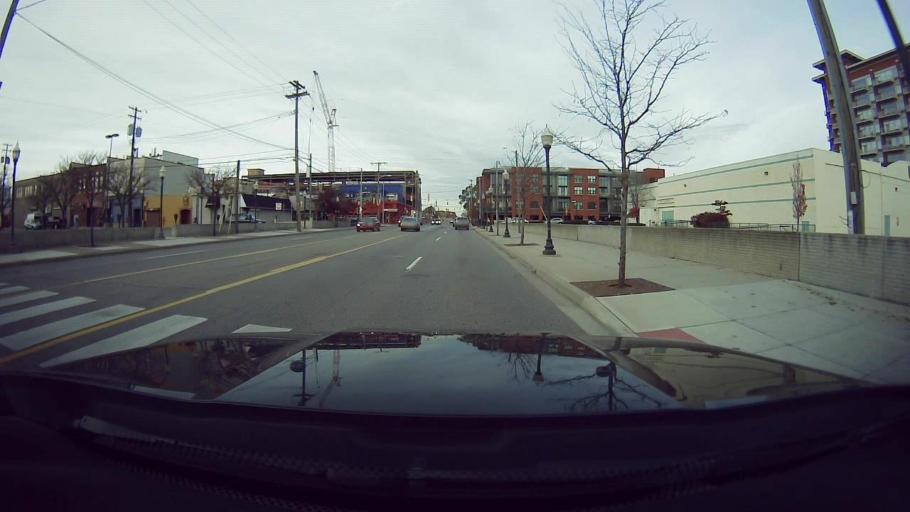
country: US
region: Michigan
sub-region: Oakland County
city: Royal Oak
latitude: 42.4899
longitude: -83.1430
